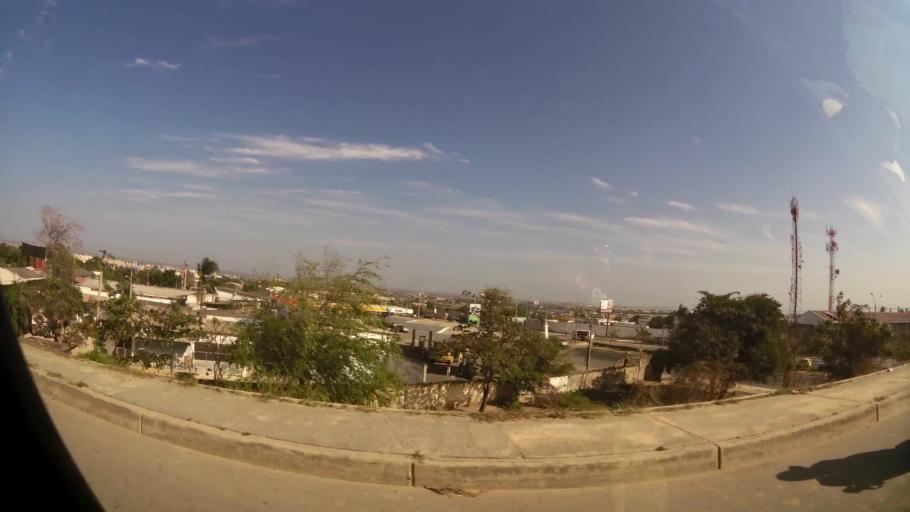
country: CO
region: Atlantico
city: Soledad
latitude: 10.9235
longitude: -74.8159
